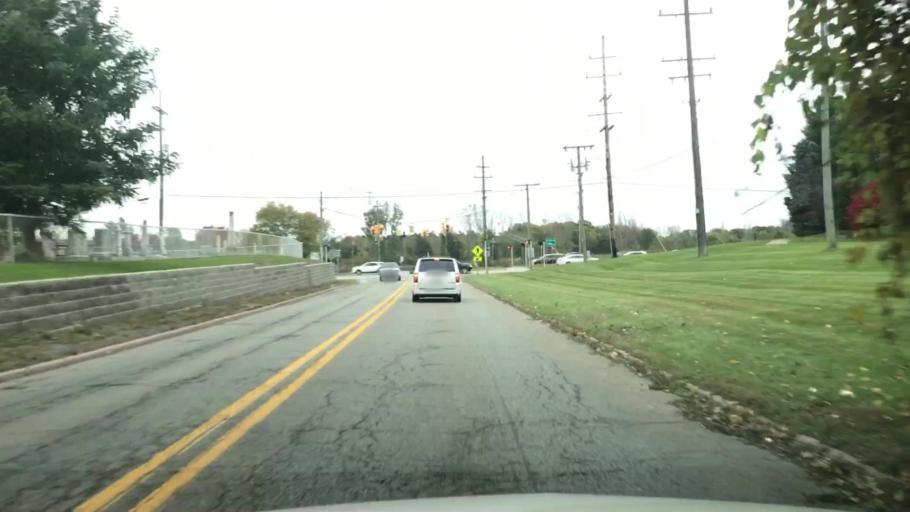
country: US
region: Michigan
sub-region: Macomb County
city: Shelby
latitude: 42.7139
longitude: -83.0560
